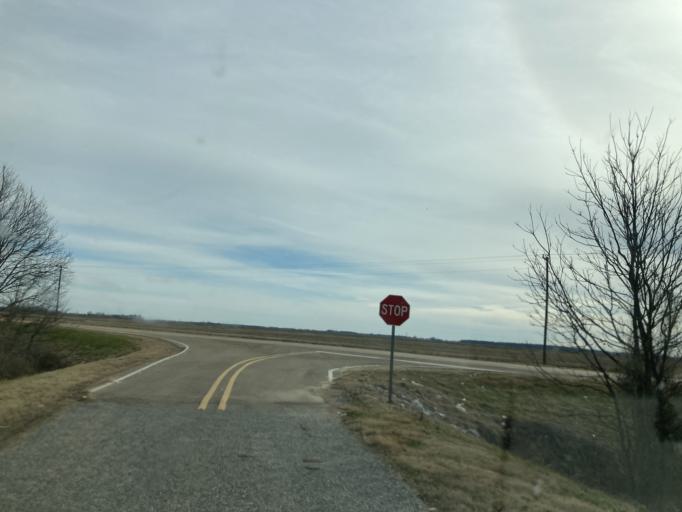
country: US
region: Mississippi
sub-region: Humphreys County
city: Belzoni
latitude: 33.1830
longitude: -90.6327
